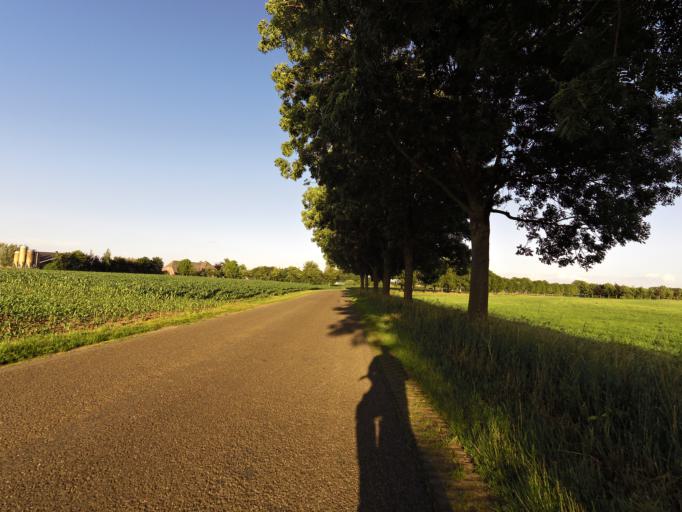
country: NL
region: Gelderland
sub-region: Oude IJsselstreek
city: Gendringen
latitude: 51.8703
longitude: 6.4263
